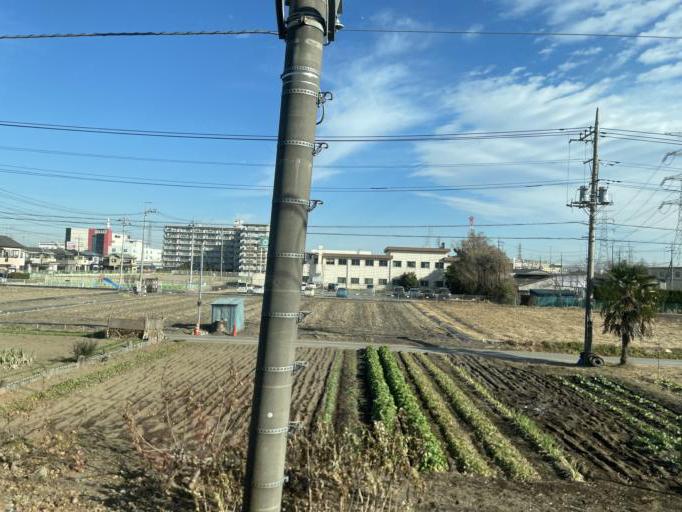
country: JP
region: Saitama
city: Konosu
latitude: 36.0761
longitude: 139.4896
